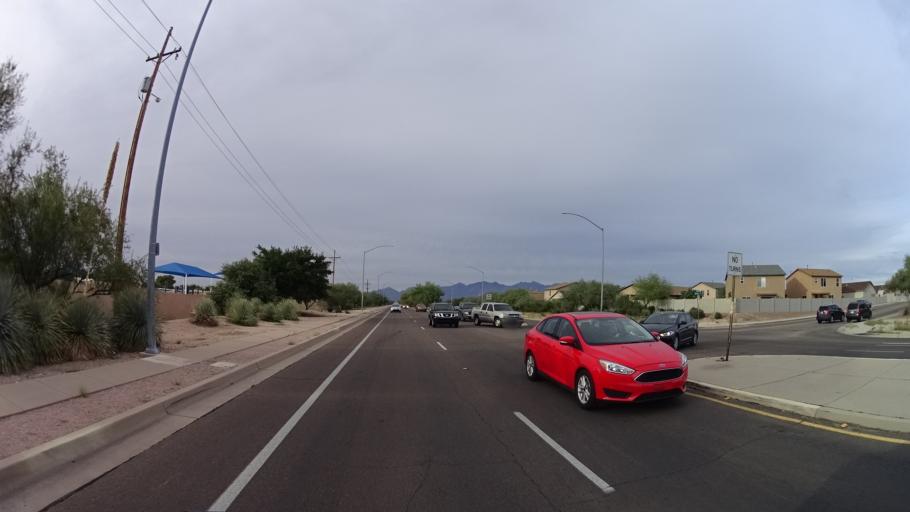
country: US
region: Arizona
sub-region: Pima County
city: South Tucson
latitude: 32.1559
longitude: -110.9351
